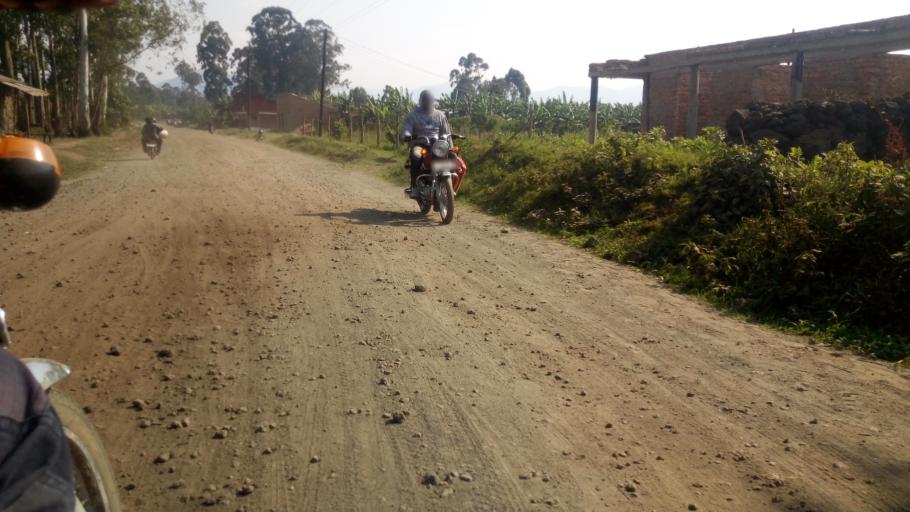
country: UG
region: Western Region
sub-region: Kisoro District
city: Kisoro
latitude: -1.2513
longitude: 29.7139
